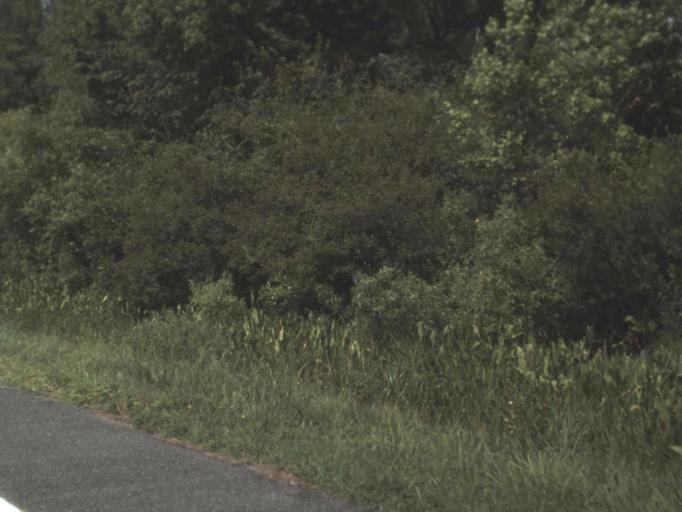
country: US
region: Florida
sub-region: Taylor County
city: Steinhatchee
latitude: 29.8601
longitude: -83.3087
